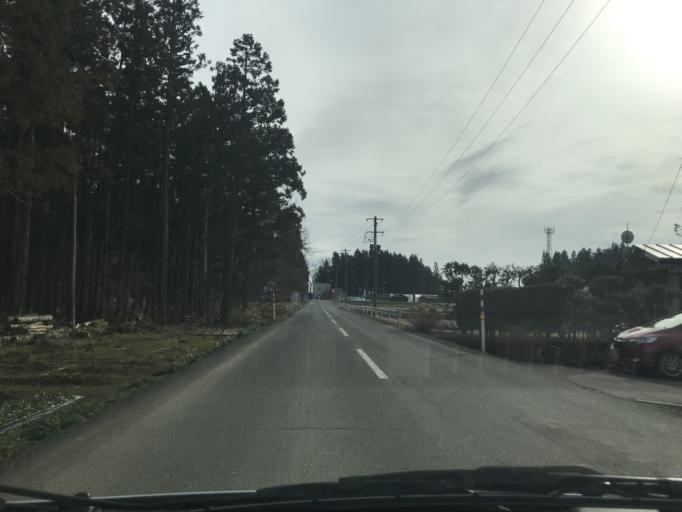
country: JP
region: Iwate
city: Hanamaki
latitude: 39.4076
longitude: 141.0776
